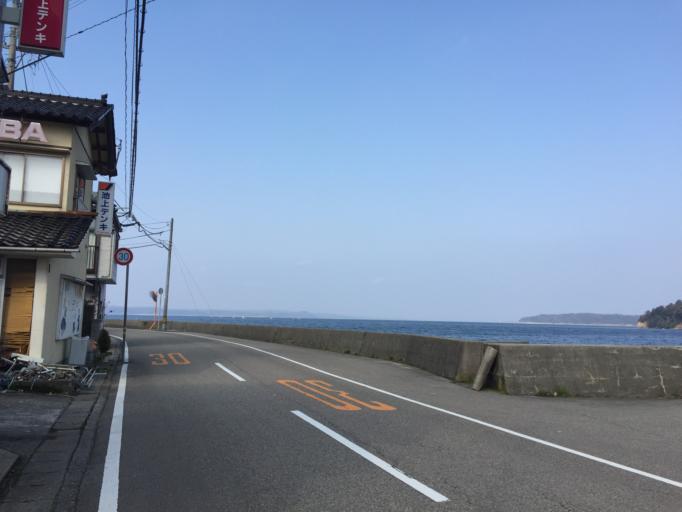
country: JP
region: Ishikawa
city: Nanao
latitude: 37.1380
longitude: 137.0000
